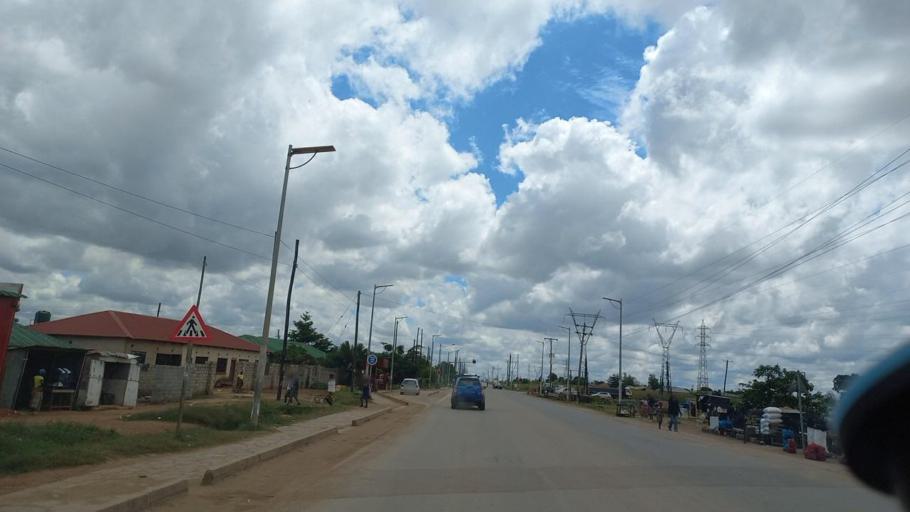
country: ZM
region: Lusaka
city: Lusaka
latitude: -15.4503
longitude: 28.3149
